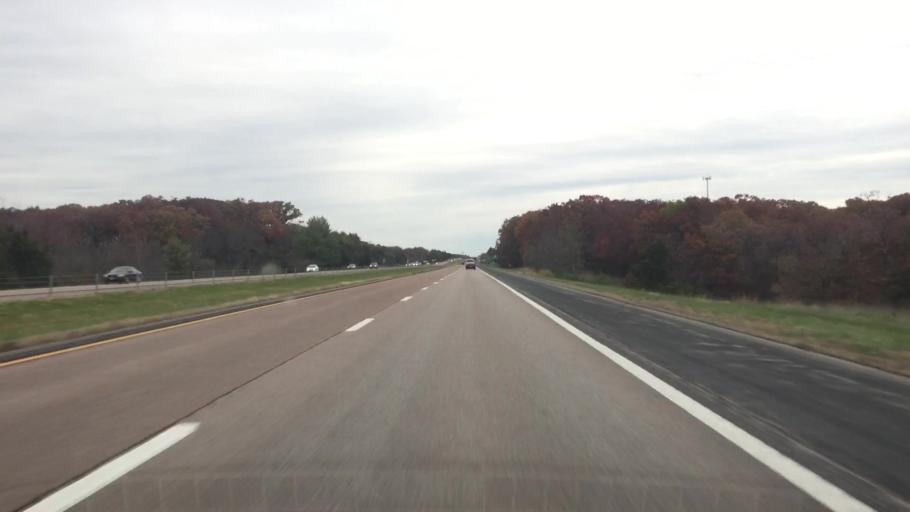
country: US
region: Missouri
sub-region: Boone County
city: Ashland
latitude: 38.7252
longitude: -92.2540
